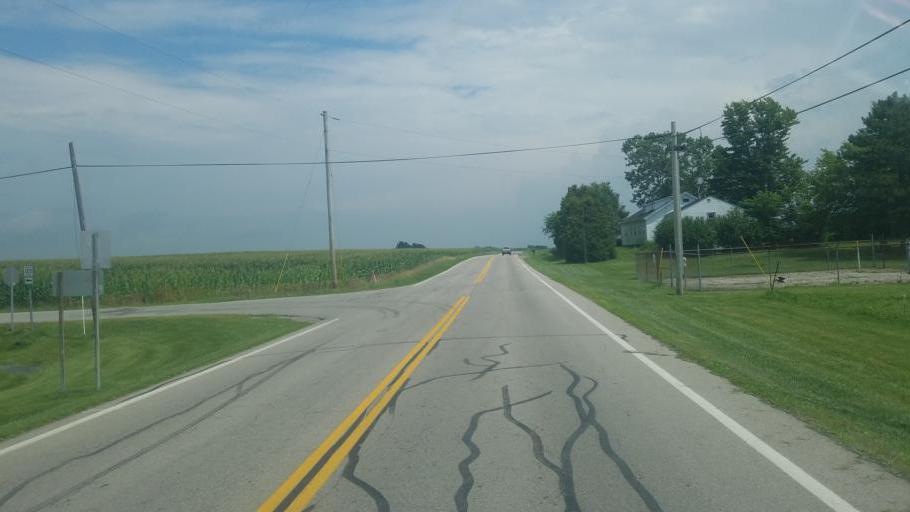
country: US
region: Ohio
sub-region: Champaign County
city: North Lewisburg
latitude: 40.4021
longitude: -83.5345
